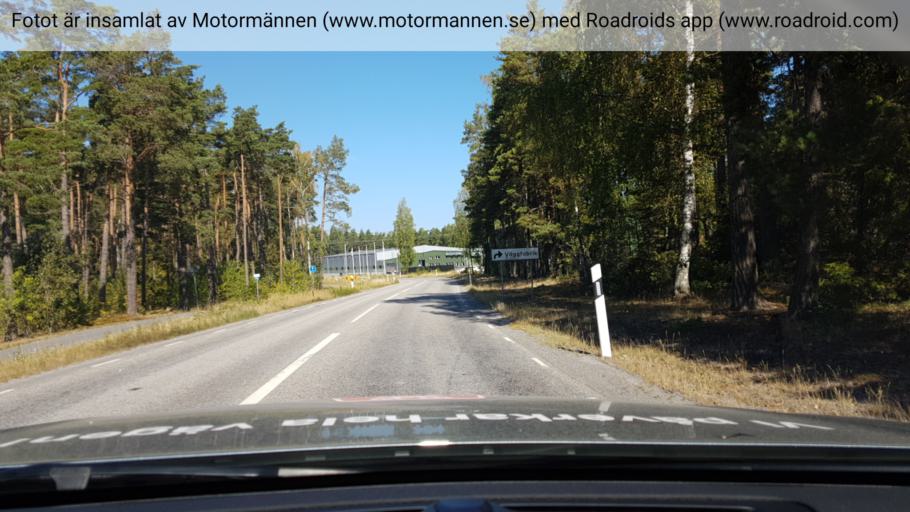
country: SE
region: Stockholm
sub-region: Ekero Kommun
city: Ekeroe
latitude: 59.2793
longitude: 17.7556
